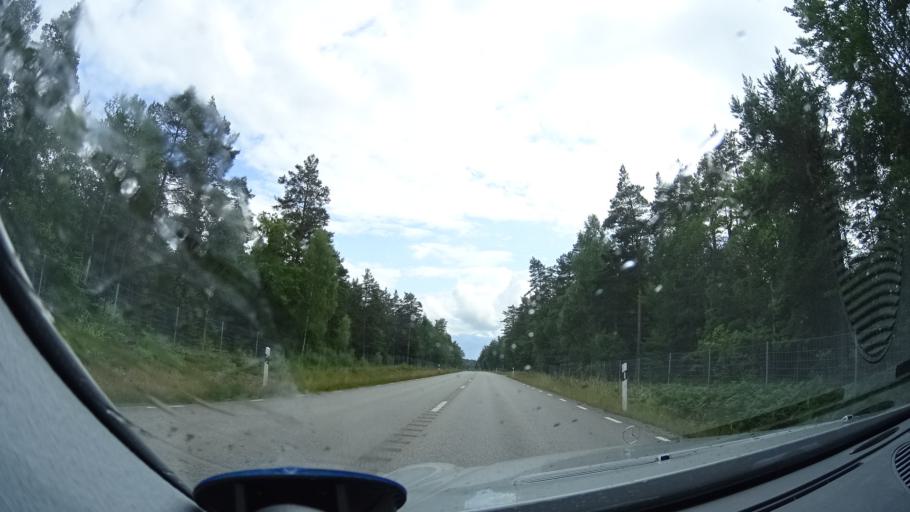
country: SE
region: Blekinge
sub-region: Karlshamns Kommun
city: Svangsta
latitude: 56.2458
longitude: 14.8283
